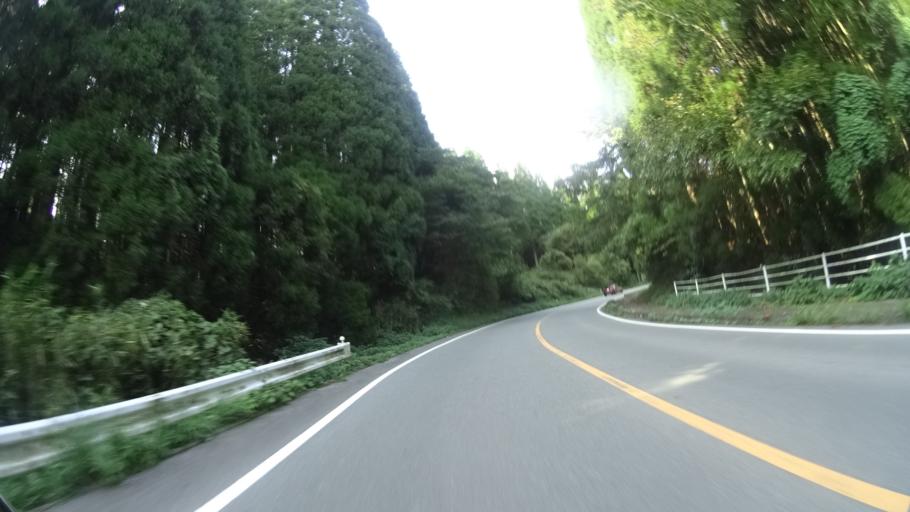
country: JP
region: Oita
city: Tsukawaki
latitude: 33.1332
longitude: 131.0865
